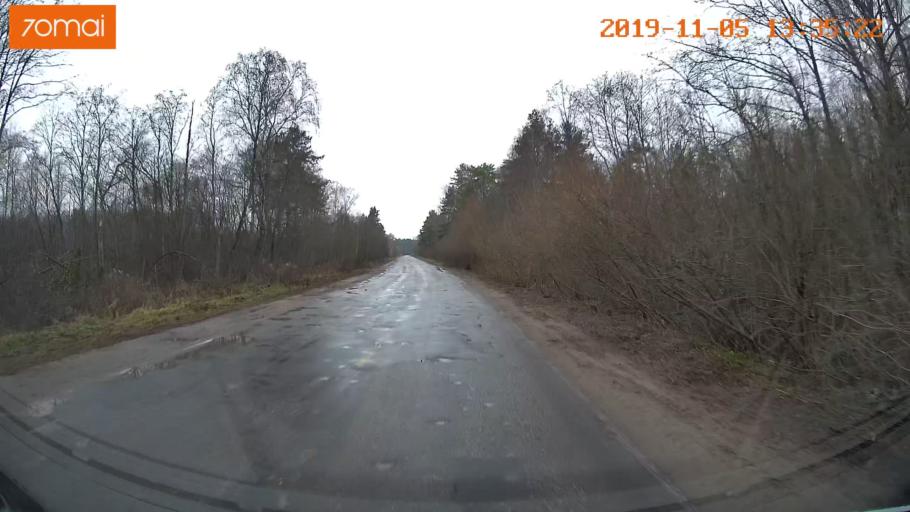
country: RU
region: Ivanovo
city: Shuya
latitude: 56.9074
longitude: 41.3879
